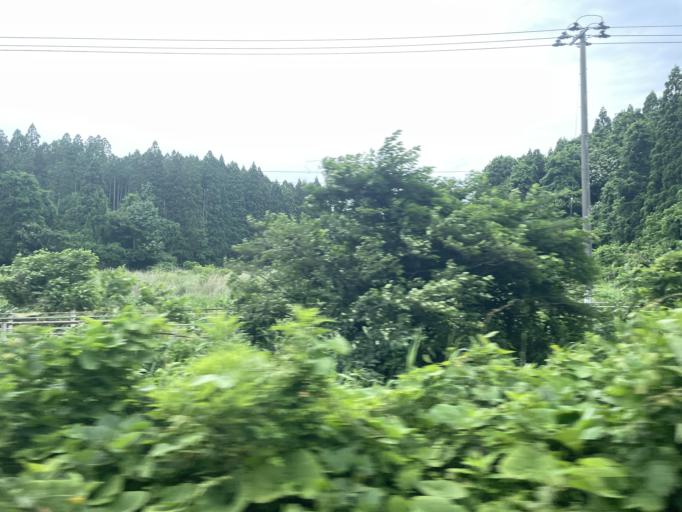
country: JP
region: Akita
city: Tenno
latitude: 39.9020
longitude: 139.8590
